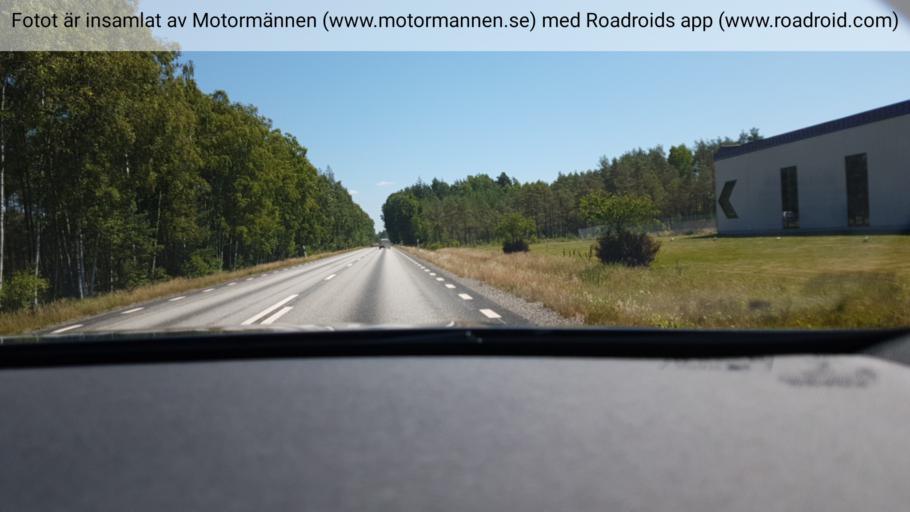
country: SE
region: Joenkoeping
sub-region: Gnosjo Kommun
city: Hillerstorp
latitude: 57.3182
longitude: 13.8954
